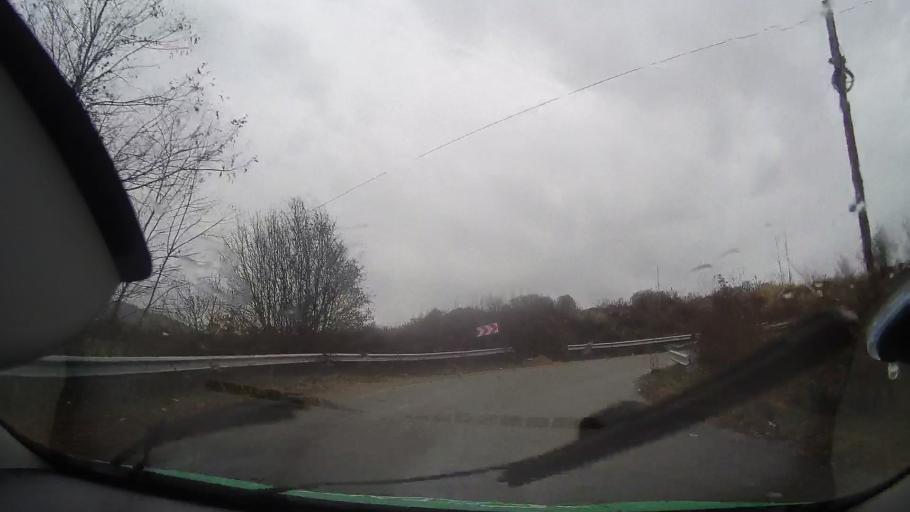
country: RO
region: Bihor
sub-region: Comuna Rabagani
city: Rabagani
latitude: 46.7270
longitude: 22.2398
